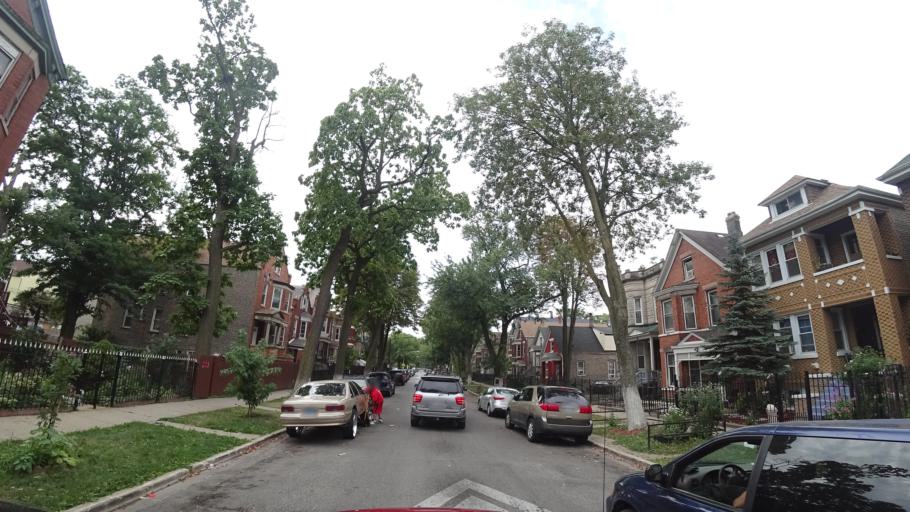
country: US
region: Illinois
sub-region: Cook County
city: Cicero
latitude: 41.8493
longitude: -87.7137
